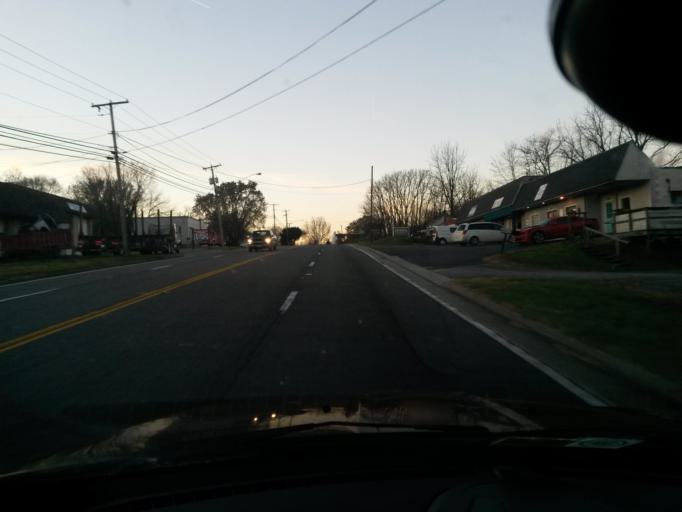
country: US
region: Virginia
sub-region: Botetourt County
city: Fincastle
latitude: 37.5020
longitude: -79.8785
